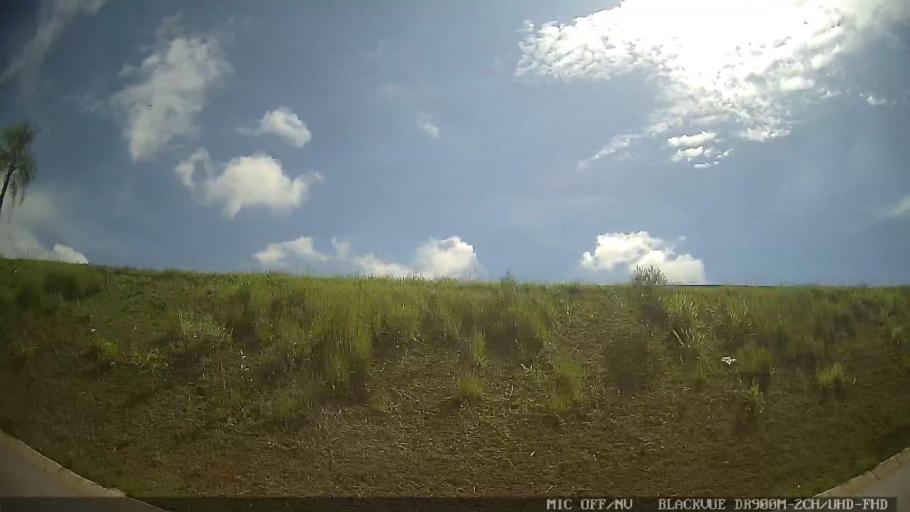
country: BR
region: Sao Paulo
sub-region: Tiete
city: Tiete
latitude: -23.1199
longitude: -47.7015
